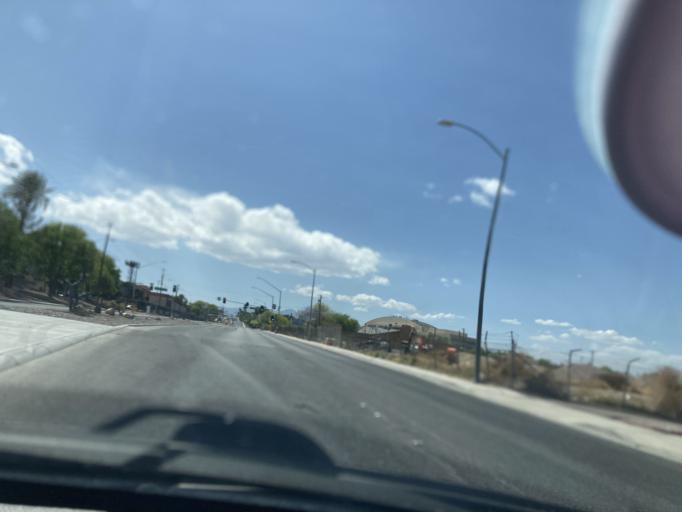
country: US
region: Nevada
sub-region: Clark County
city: Las Vegas
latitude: 36.1813
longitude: -115.1267
